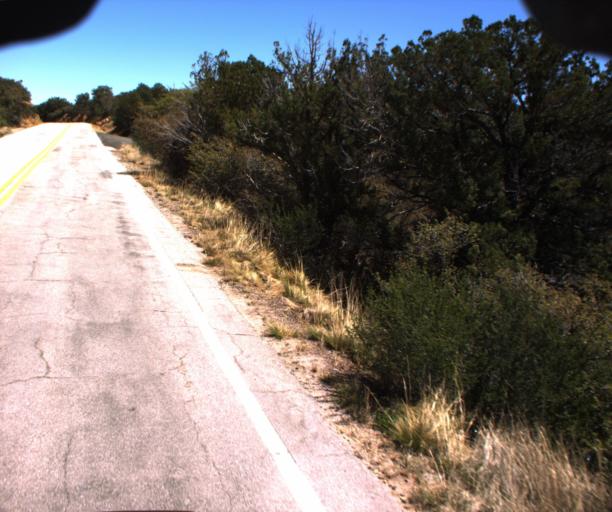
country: US
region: Arizona
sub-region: Yavapai County
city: Prescott
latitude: 34.4287
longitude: -112.5469
